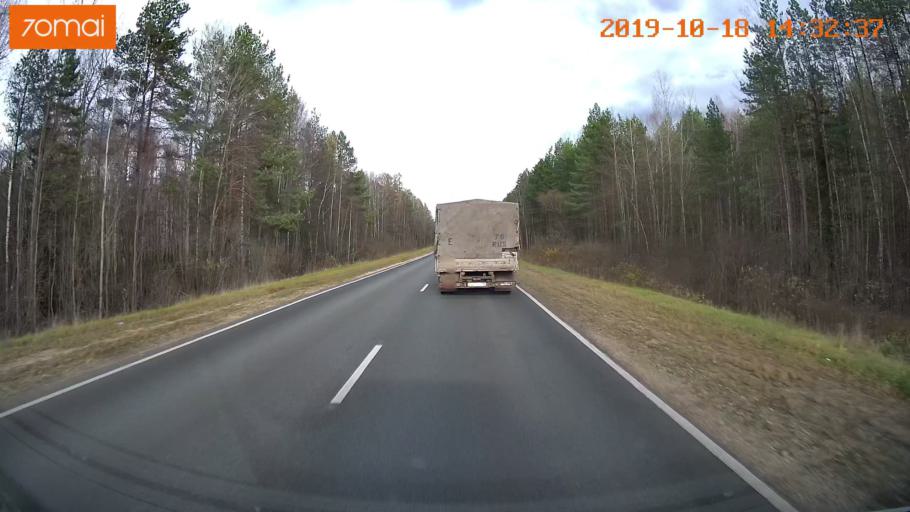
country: RU
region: Rjazan
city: Tuma
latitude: 55.1932
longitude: 40.5831
